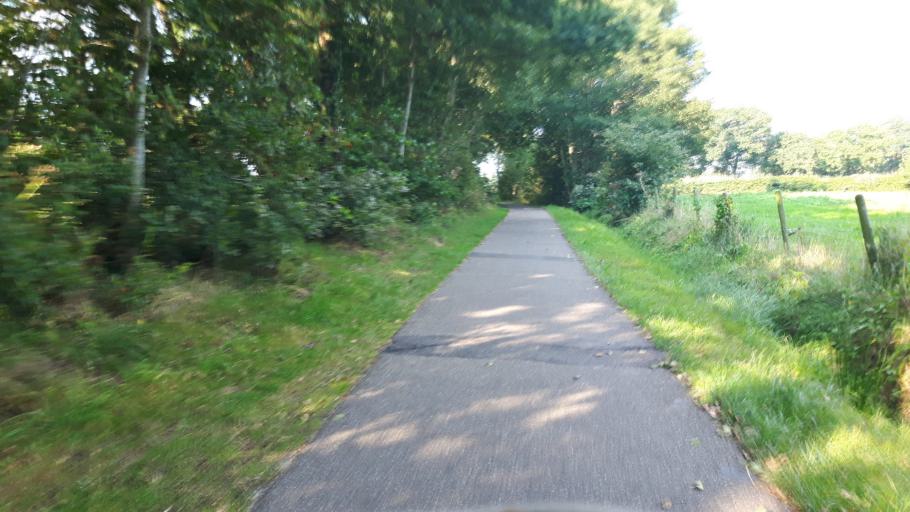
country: NL
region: Groningen
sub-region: Gemeente Leek
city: Leek
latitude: 53.1372
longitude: 6.4436
